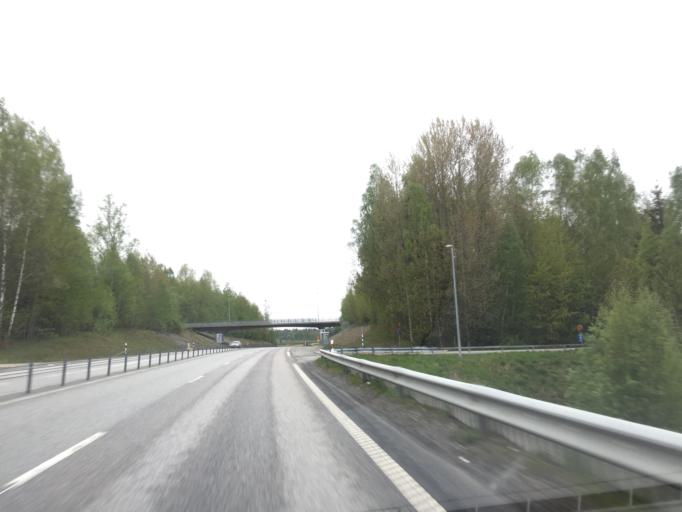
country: SE
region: OErebro
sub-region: Orebro Kommun
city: Hovsta
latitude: 59.3650
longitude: 15.2242
